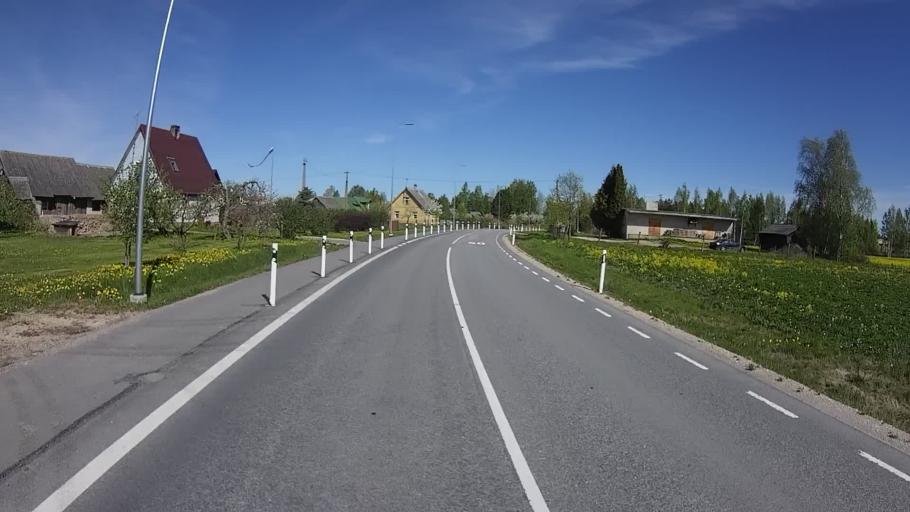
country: EE
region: Polvamaa
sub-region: Raepina vald
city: Rapina
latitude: 57.9995
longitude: 27.5453
